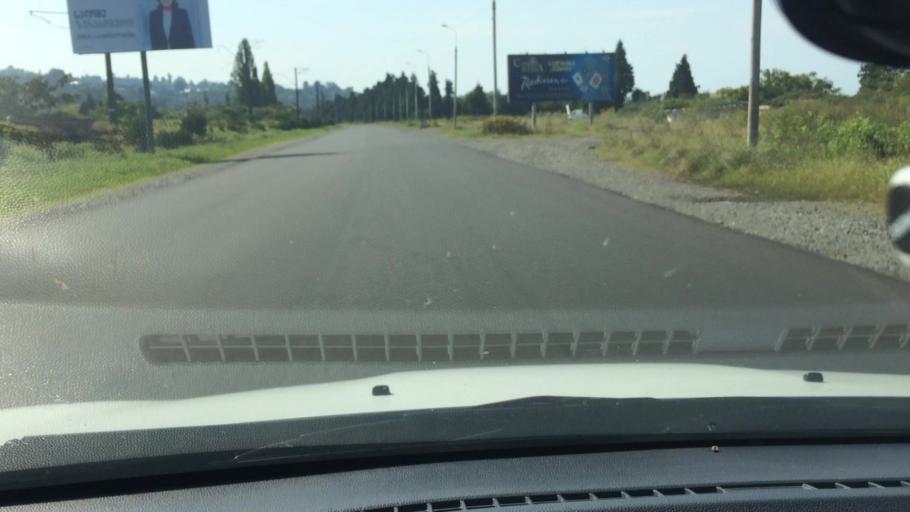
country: GE
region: Ajaria
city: Kobuleti
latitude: 41.7915
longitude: 41.7686
